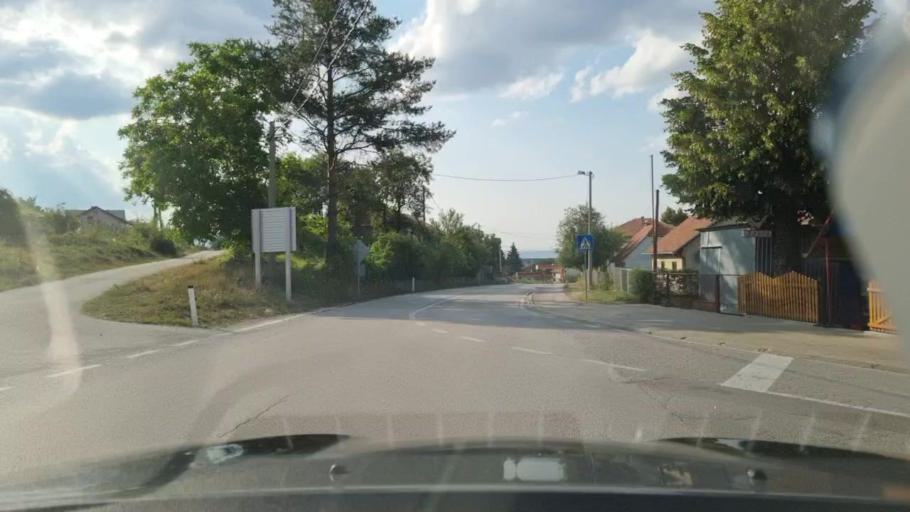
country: BA
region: Federation of Bosnia and Herzegovina
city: Glamoc
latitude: 44.0487
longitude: 16.8433
